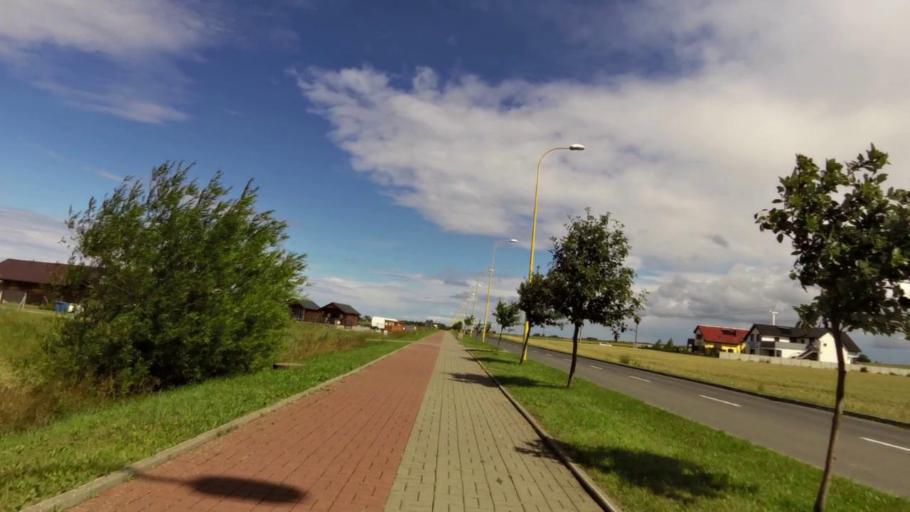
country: PL
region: West Pomeranian Voivodeship
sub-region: Powiat slawienski
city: Darlowo
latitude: 54.4365
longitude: 16.4096
